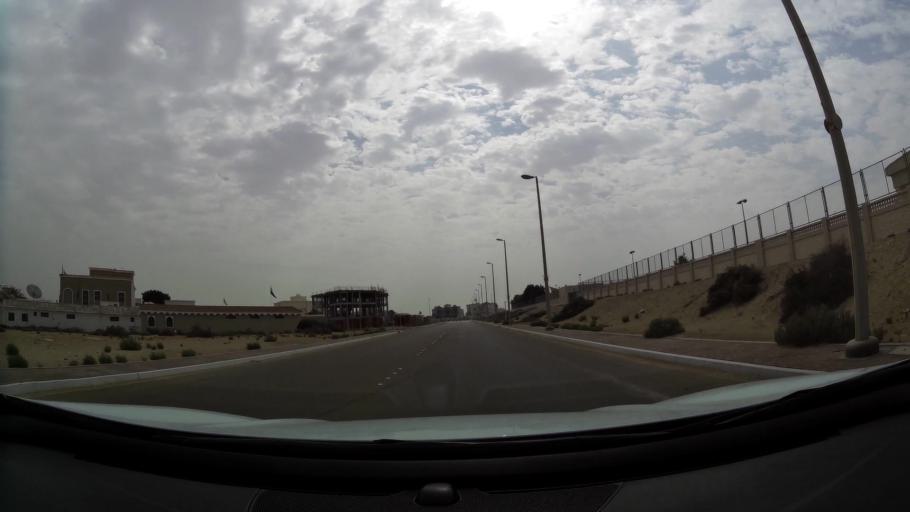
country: AE
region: Abu Dhabi
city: Abu Dhabi
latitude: 24.3159
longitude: 54.6444
